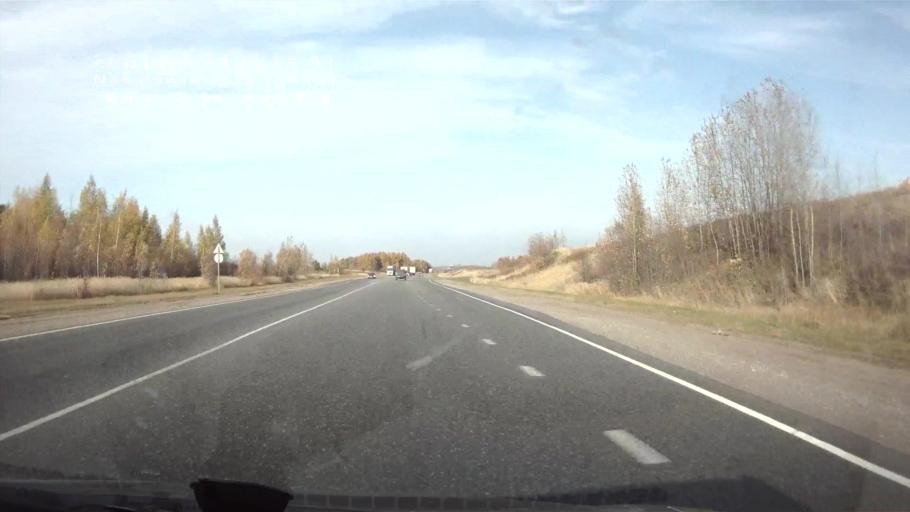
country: RU
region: Chuvashia
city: Kugesi
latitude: 56.0448
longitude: 47.3687
